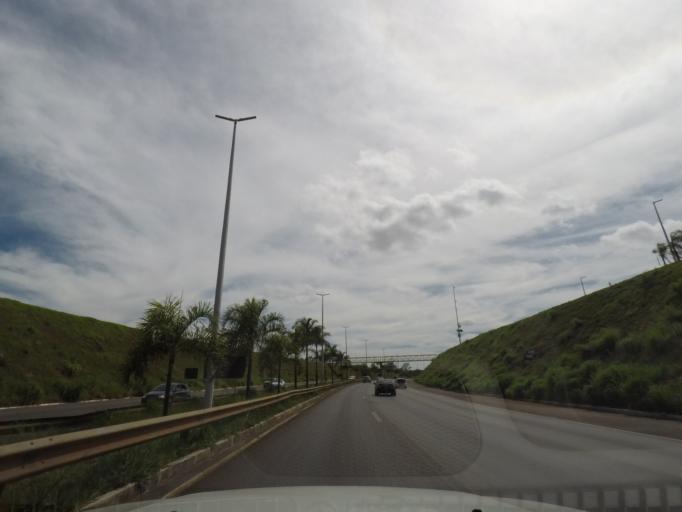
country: BR
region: Federal District
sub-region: Brasilia
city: Brasilia
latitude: -15.6888
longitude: -47.8605
